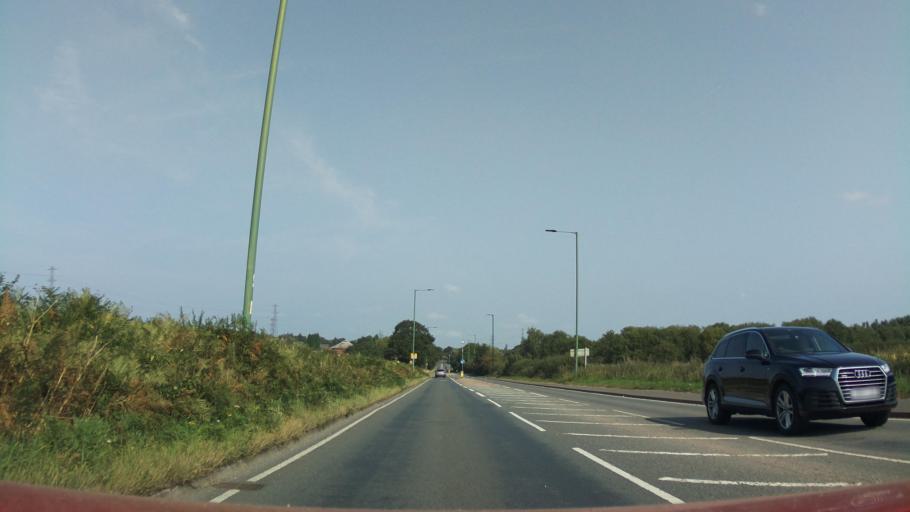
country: GB
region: England
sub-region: Walsall
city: Streetly
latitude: 52.5931
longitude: -1.8901
